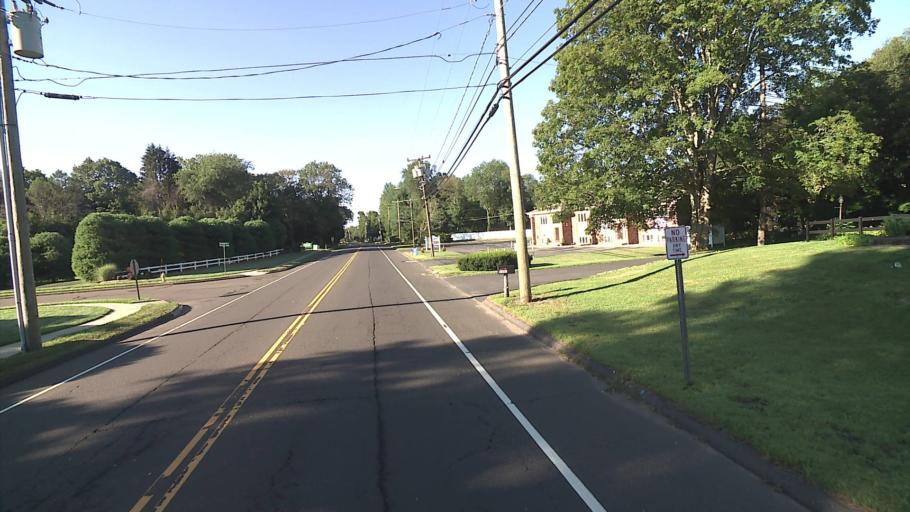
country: US
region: Connecticut
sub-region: New Haven County
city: Cheshire
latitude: 41.4735
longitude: -72.9067
